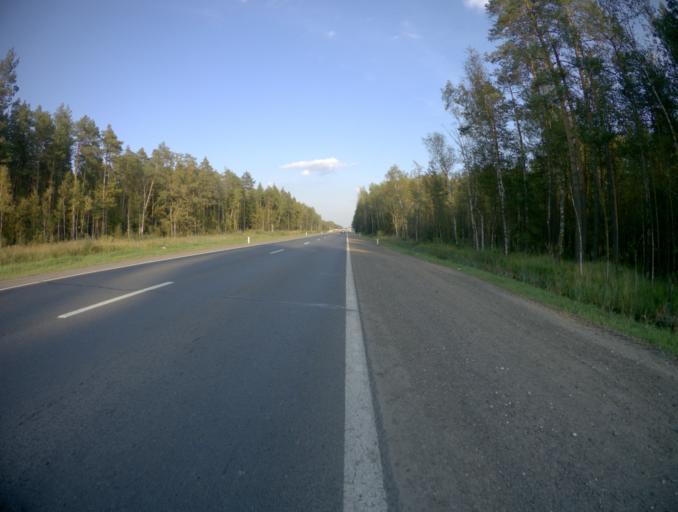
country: RU
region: Vladimir
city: Kameshkovo
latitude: 56.1935
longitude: 40.9377
